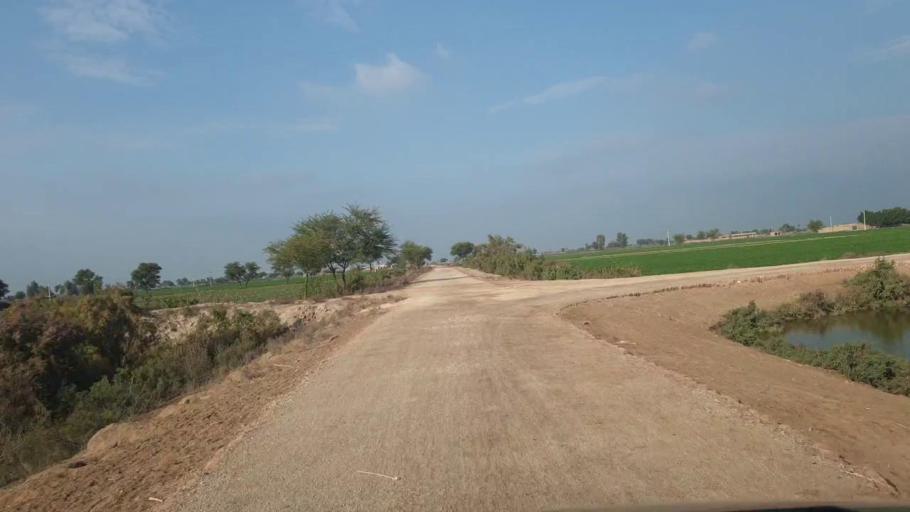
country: PK
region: Sindh
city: Shahdadpur
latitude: 25.8940
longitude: 68.6706
